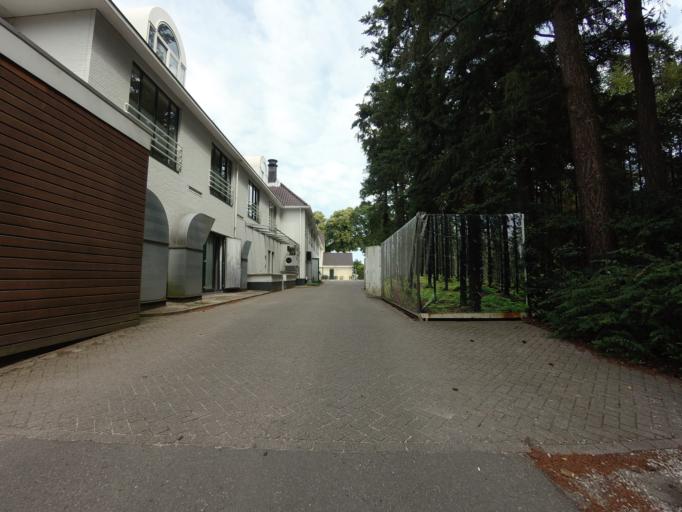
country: NL
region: Utrecht
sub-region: Gemeente Utrechtse Heuvelrug
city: Driebergen-Rijsenburg
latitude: 52.0901
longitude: 5.2841
